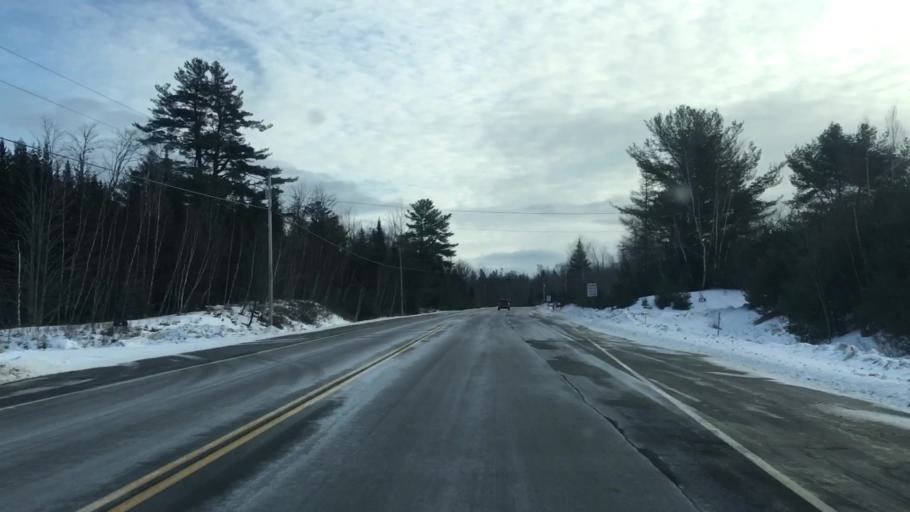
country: US
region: Maine
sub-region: Washington County
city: Machias
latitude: 44.9503
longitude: -67.6755
